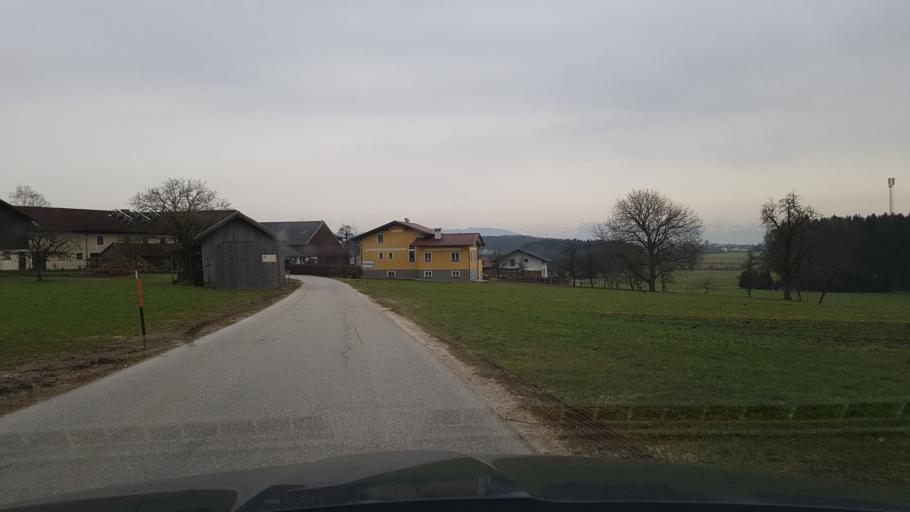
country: AT
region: Salzburg
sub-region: Politischer Bezirk Salzburg-Umgebung
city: Lamprechtshausen
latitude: 48.0125
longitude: 12.9583
